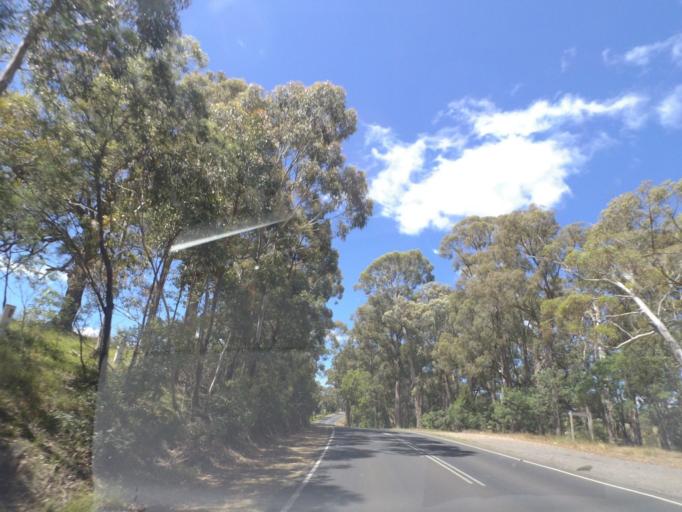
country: AU
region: Victoria
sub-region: Mount Alexander
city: Castlemaine
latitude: -37.2901
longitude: 144.2672
